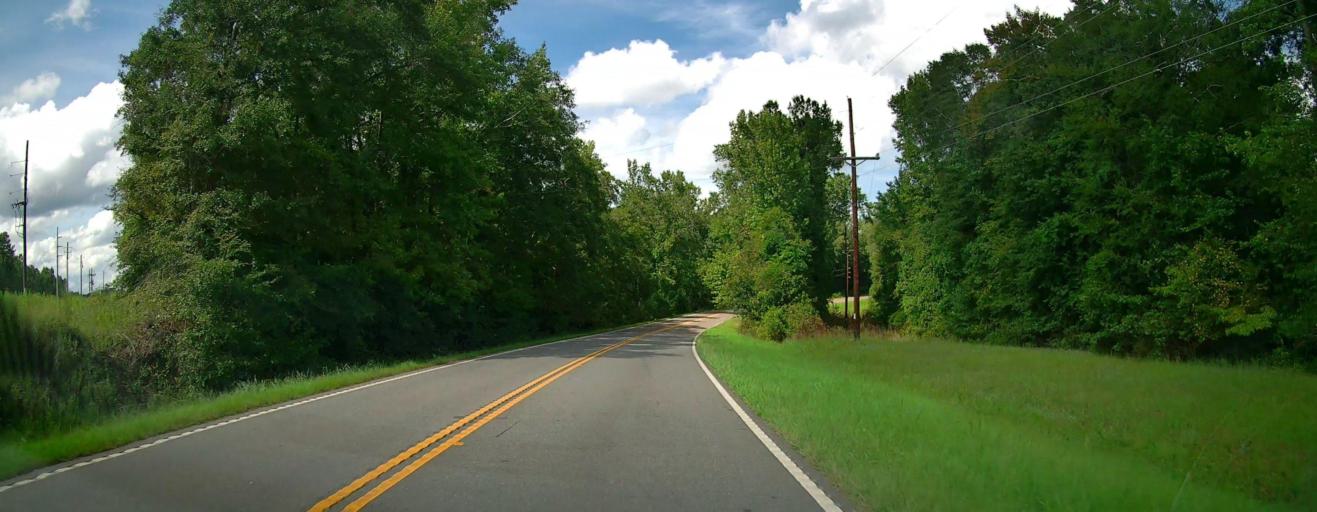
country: US
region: Georgia
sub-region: Talbot County
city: Talbotton
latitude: 32.6205
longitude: -84.4885
